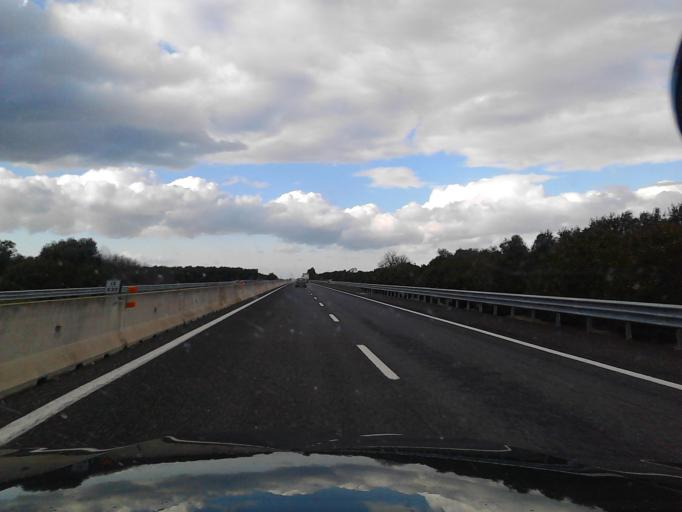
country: IT
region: Apulia
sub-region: Provincia di Barletta - Andria - Trani
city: Trani
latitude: 41.2411
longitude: 16.3598
